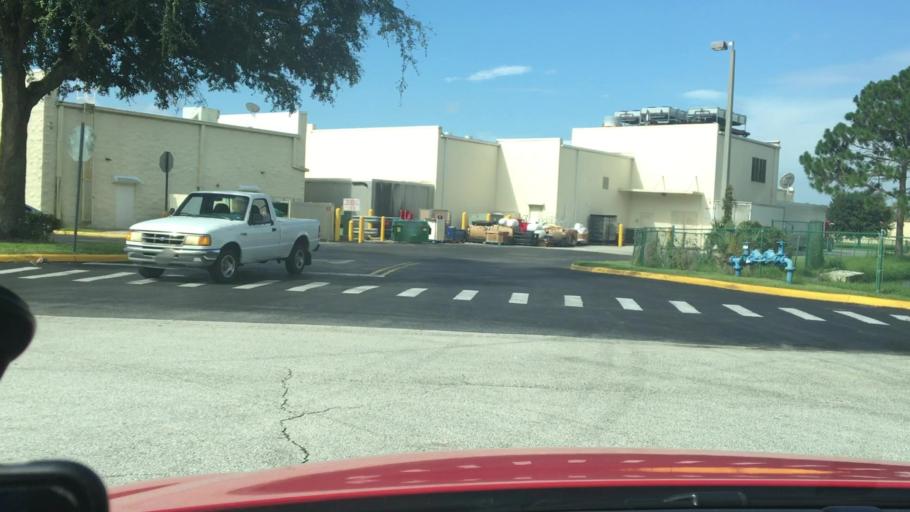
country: US
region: Florida
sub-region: Volusia County
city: New Smyrna Beach
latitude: 29.0170
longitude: -80.9435
